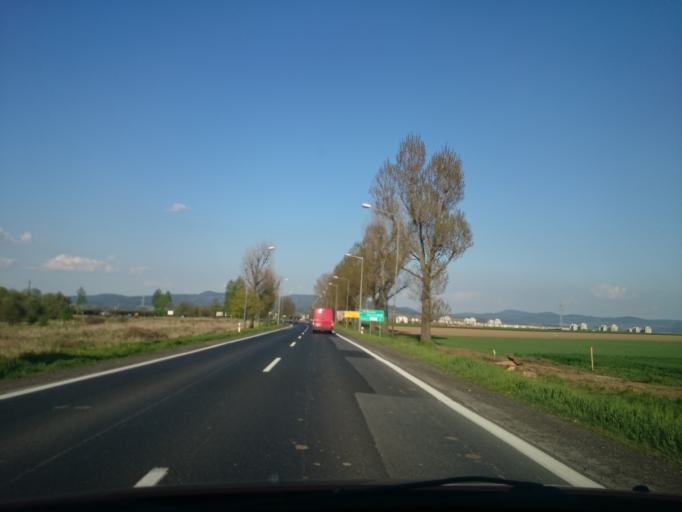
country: PL
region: Lower Silesian Voivodeship
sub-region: Powiat klodzki
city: Klodzko
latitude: 50.4382
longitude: 16.6203
